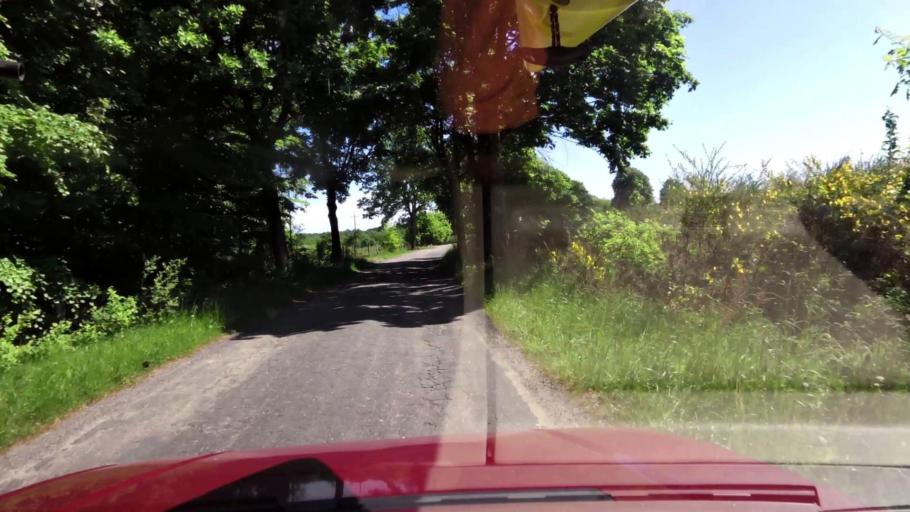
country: PL
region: West Pomeranian Voivodeship
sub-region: Powiat koszalinski
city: Polanow
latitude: 54.0399
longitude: 16.7601
